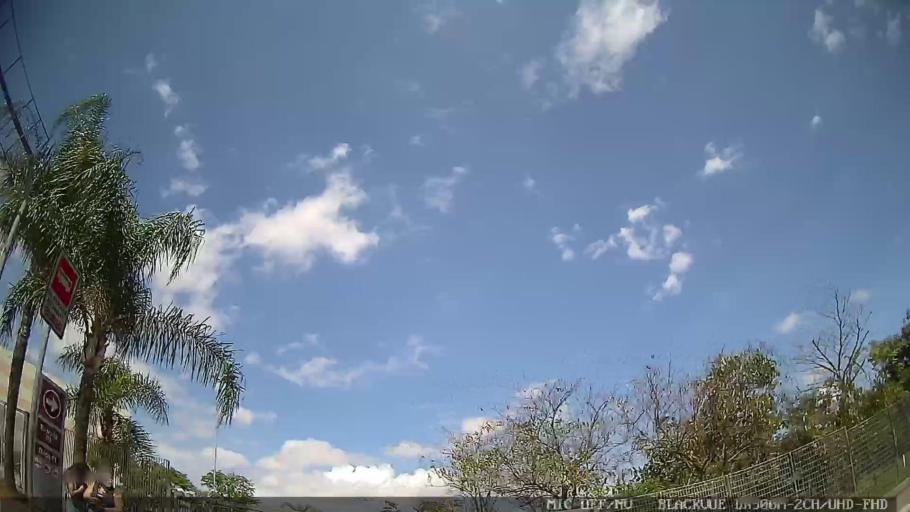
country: BR
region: Sao Paulo
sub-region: Guarulhos
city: Guarulhos
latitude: -23.5414
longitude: -46.4727
